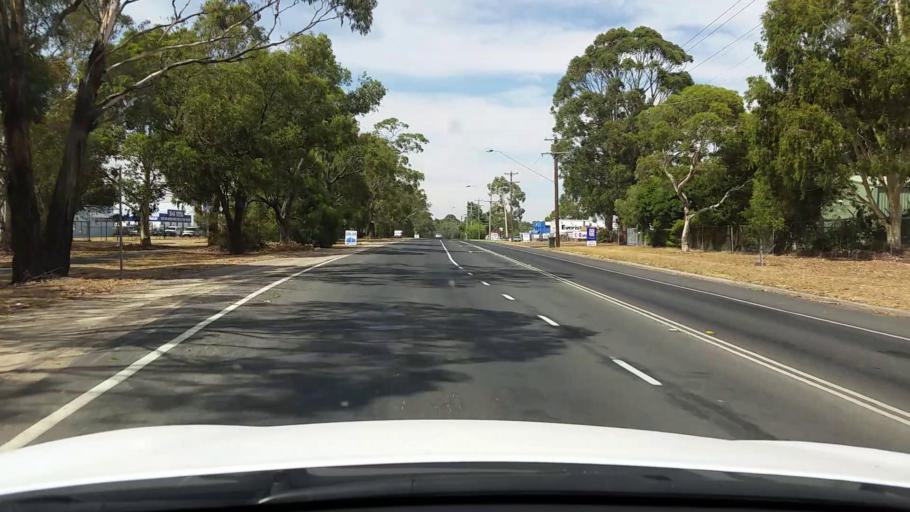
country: AU
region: Victoria
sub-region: Mornington Peninsula
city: Hastings
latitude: -38.3117
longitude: 145.1836
